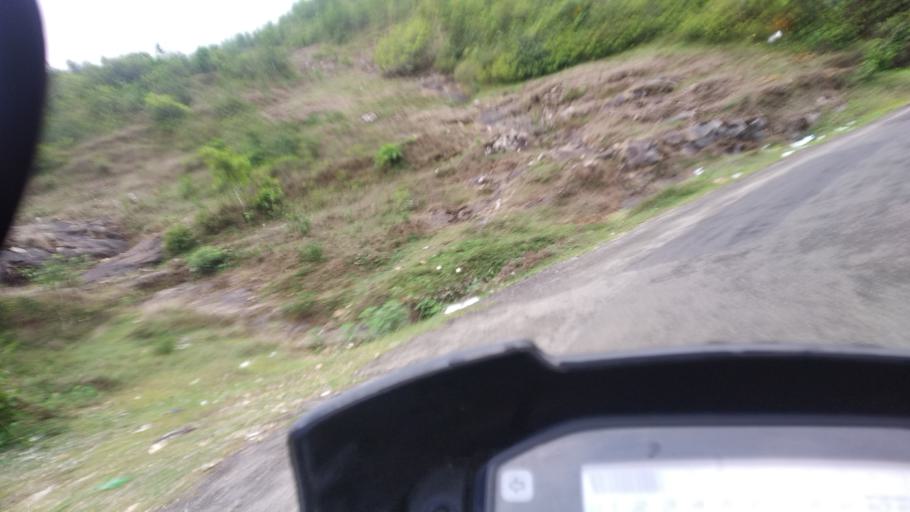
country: IN
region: Kerala
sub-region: Kottayam
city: Erattupetta
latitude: 9.6348
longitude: 76.9386
